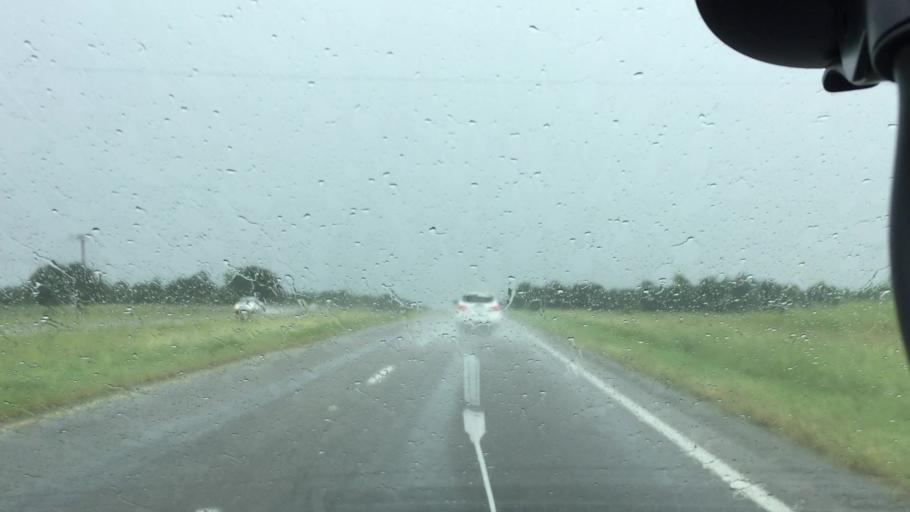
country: US
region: Alabama
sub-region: Montgomery County
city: Pike Road
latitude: 32.2189
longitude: -86.1180
